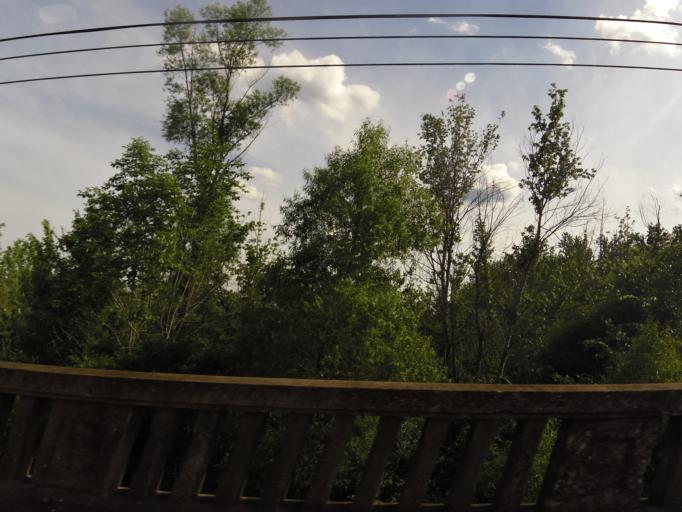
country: US
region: Tennessee
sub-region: Carroll County
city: Bruceton
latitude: 36.0367
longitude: -88.2259
